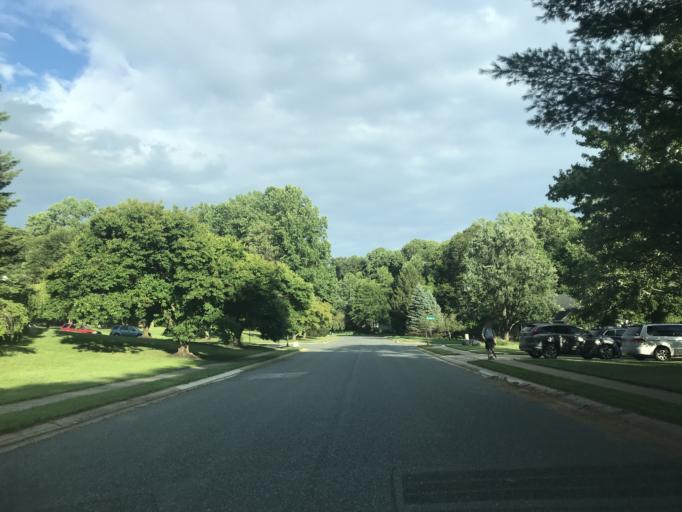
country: US
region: Maryland
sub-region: Harford County
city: South Bel Air
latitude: 39.5595
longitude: -76.3196
